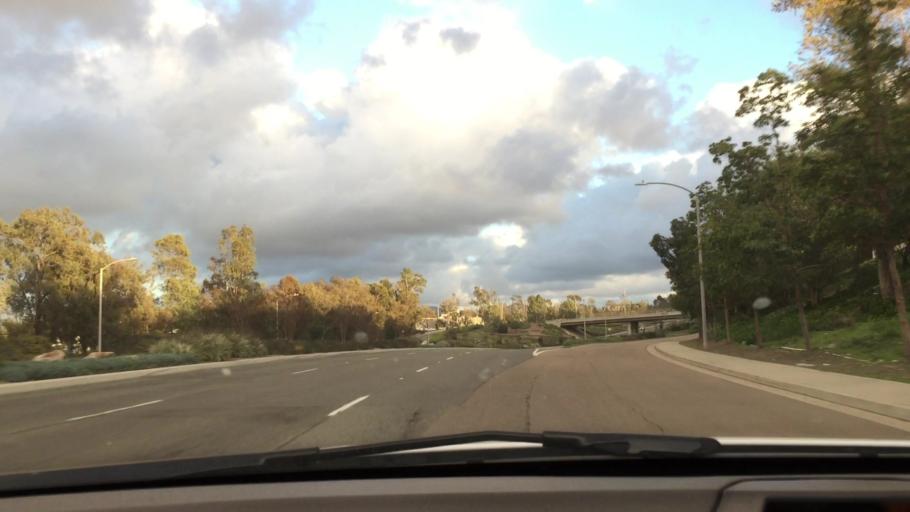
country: US
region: California
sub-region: San Diego County
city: Fairbanks Ranch
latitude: 33.0154
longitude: -117.1076
